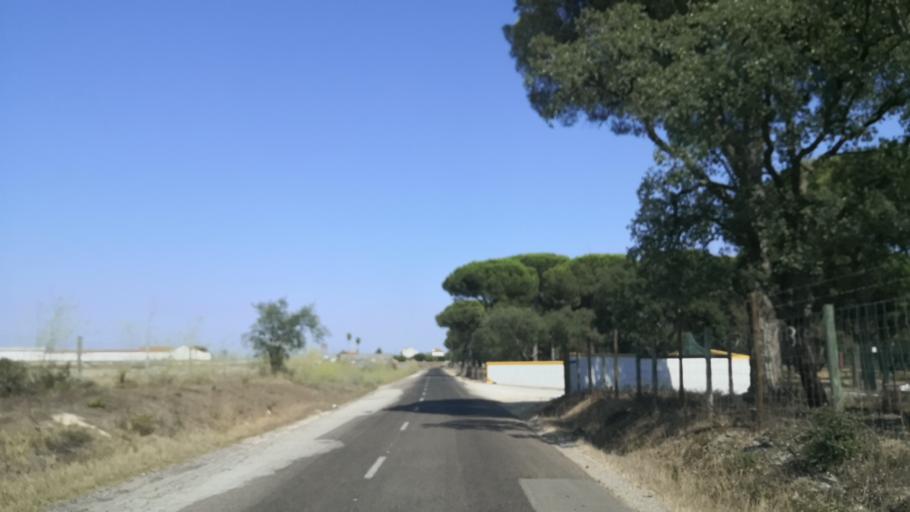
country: PT
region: Santarem
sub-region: Benavente
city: Poceirao
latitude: 38.7448
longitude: -8.6794
